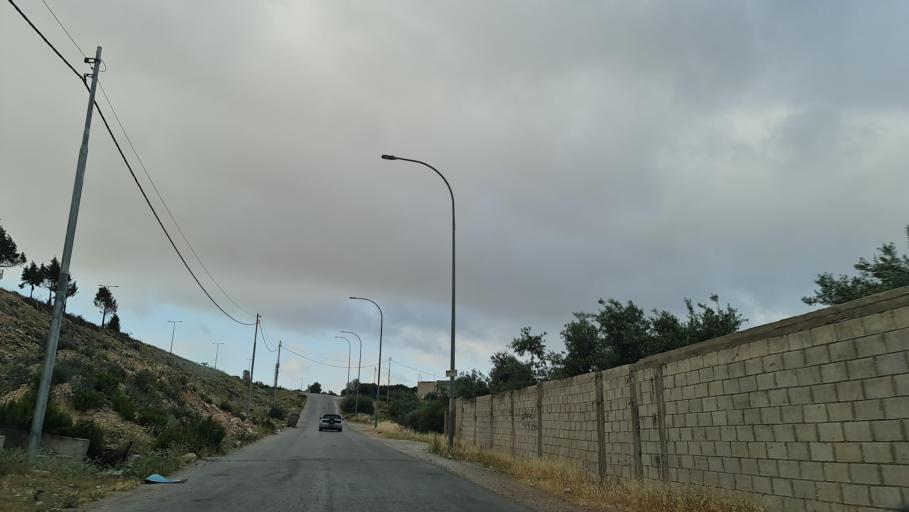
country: JO
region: Amman
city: Al Jubayhah
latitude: 32.0907
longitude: 35.8946
